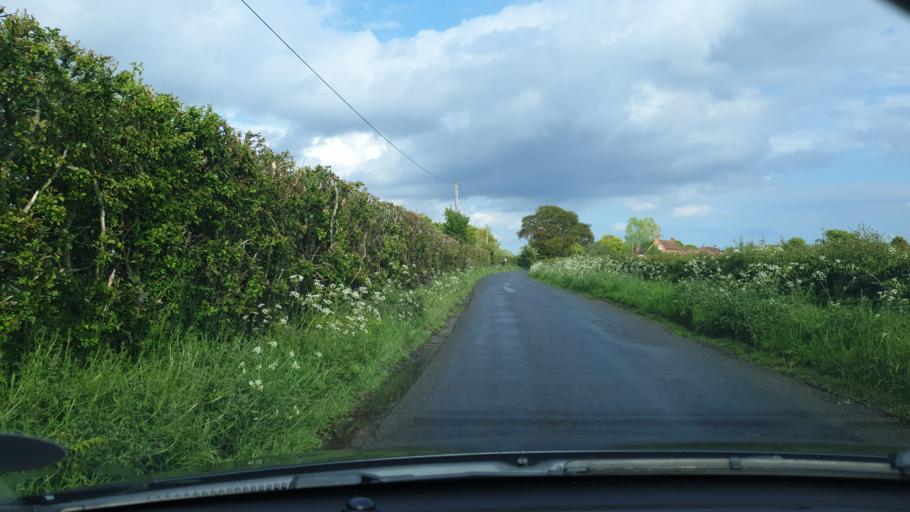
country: GB
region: England
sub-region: Essex
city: Saint Osyth
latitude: 51.8247
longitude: 1.0981
